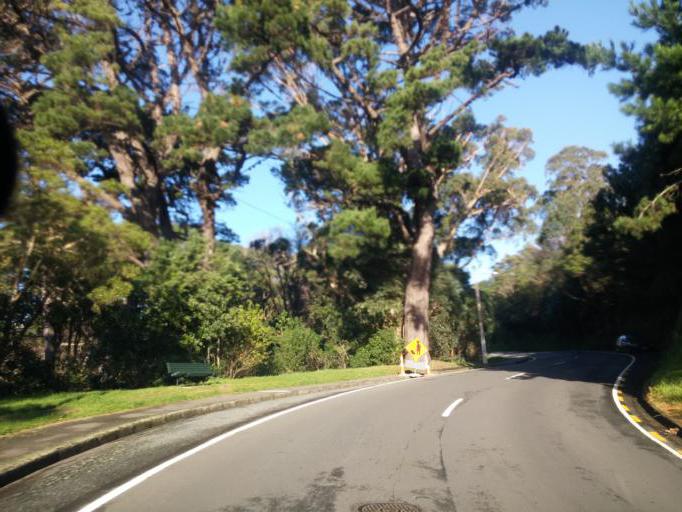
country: NZ
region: Wellington
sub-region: Wellington City
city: Wellington
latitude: -41.2982
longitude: 174.7677
